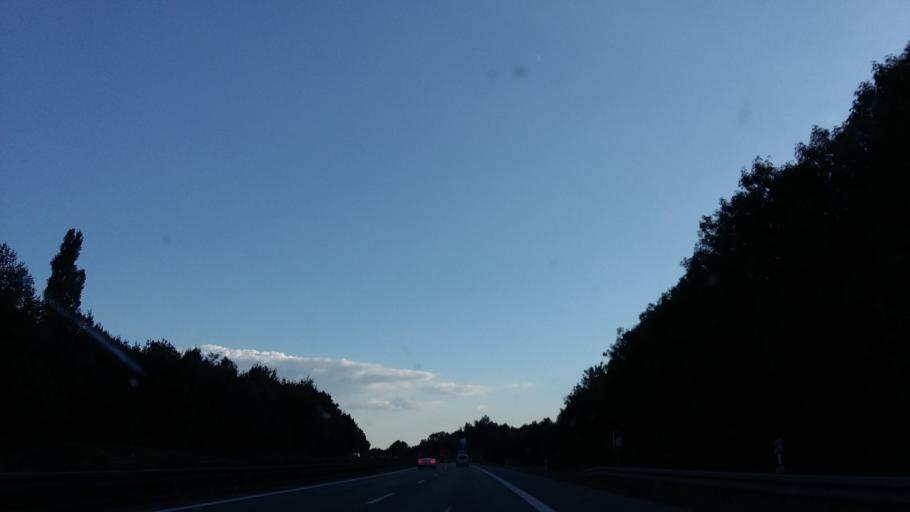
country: DE
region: Bavaria
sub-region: Swabia
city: Altenstadt
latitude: 48.1382
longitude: 10.1116
